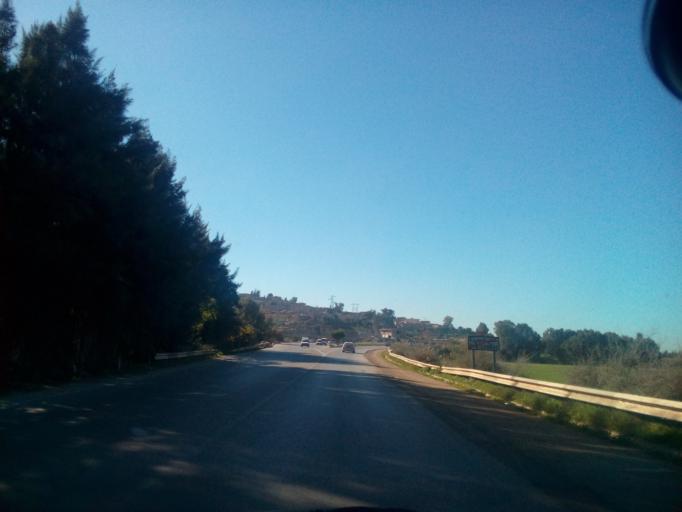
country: DZ
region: Relizane
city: Oued Rhiou
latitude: 35.9705
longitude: 0.9470
